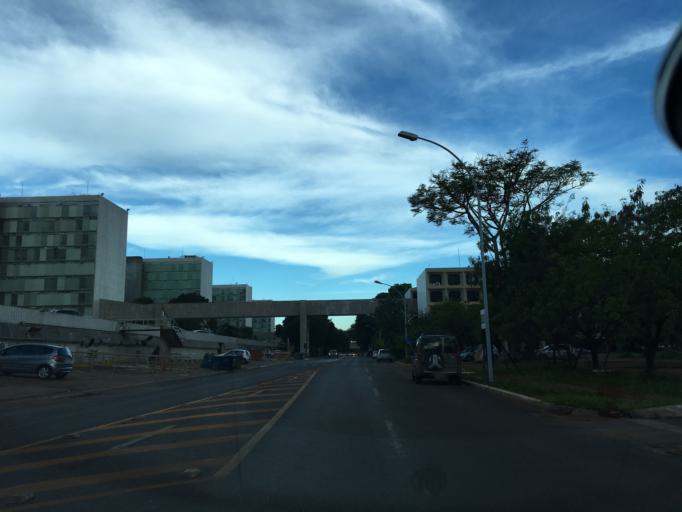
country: BR
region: Federal District
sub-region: Brasilia
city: Brasilia
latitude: -15.8001
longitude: -47.8727
